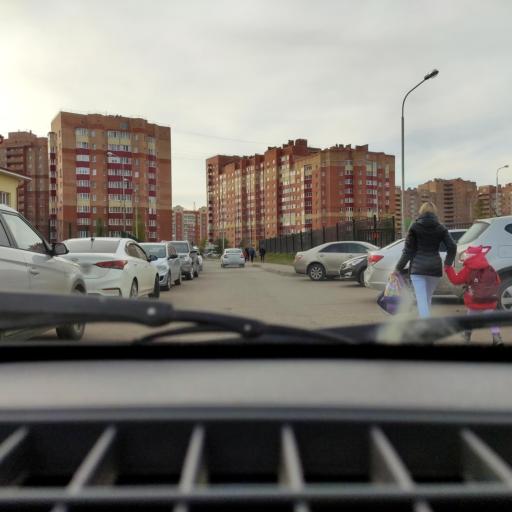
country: RU
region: Bashkortostan
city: Mikhaylovka
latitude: 54.7151
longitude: 55.8410
